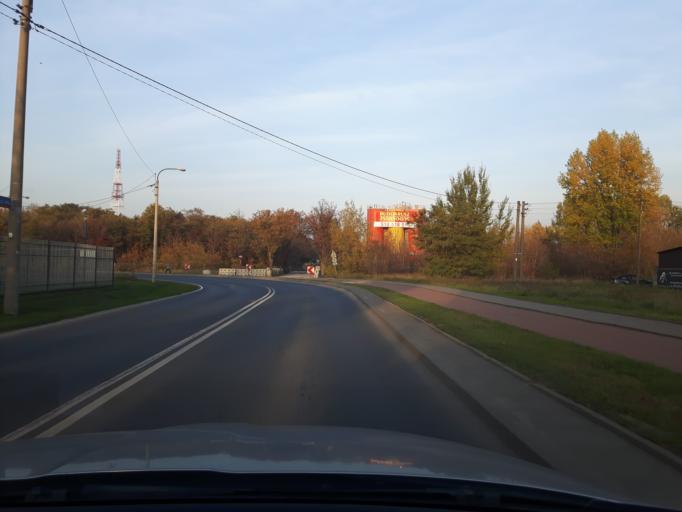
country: PL
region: Masovian Voivodeship
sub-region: Warszawa
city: Praga Poludnie
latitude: 52.2619
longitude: 21.0784
